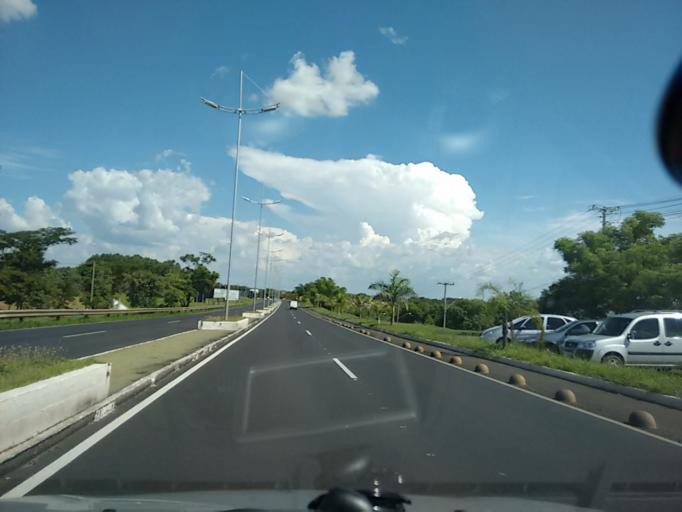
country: BR
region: Sao Paulo
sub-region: Pompeia
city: Pompeia
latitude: -22.1133
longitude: -50.1588
